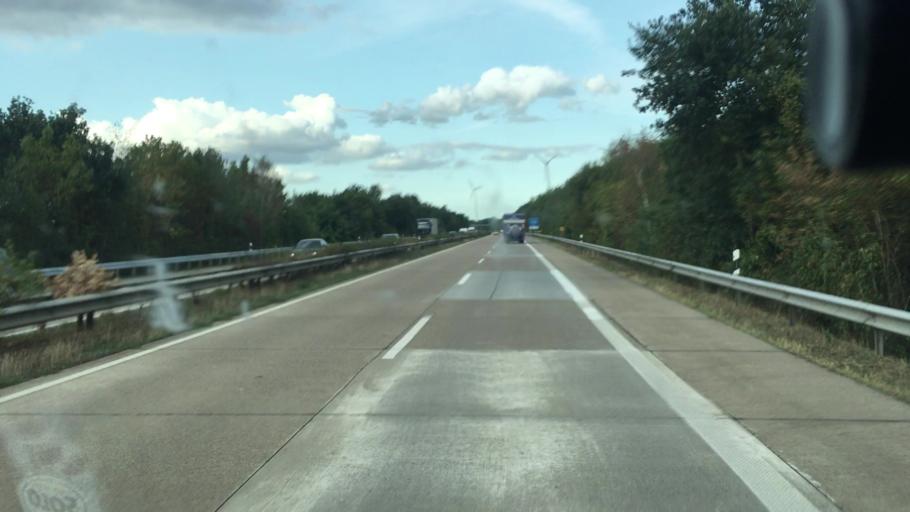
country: DE
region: Lower Saxony
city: Wardenburg
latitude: 52.9922
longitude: 8.2003
